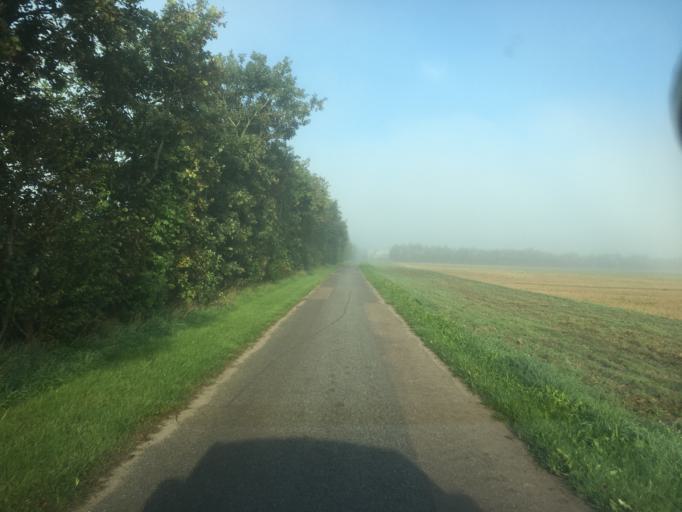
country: DK
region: South Denmark
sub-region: Tonder Kommune
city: Logumkloster
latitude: 55.0184
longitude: 8.9106
